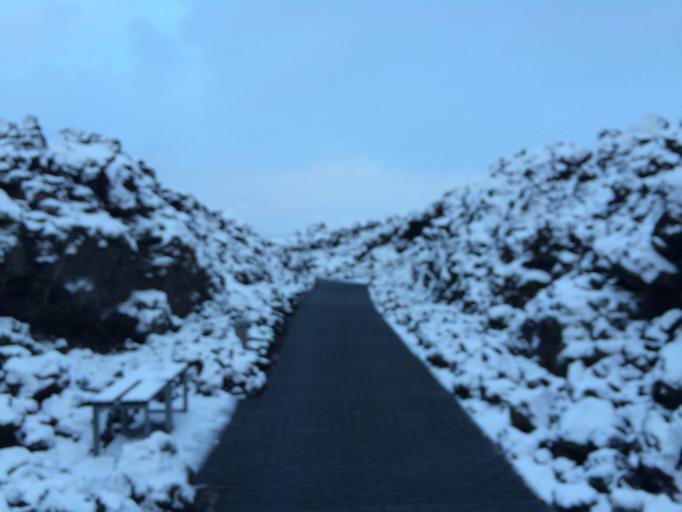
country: IS
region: Southern Peninsula
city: Grindavik
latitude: 63.8811
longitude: -22.4510
